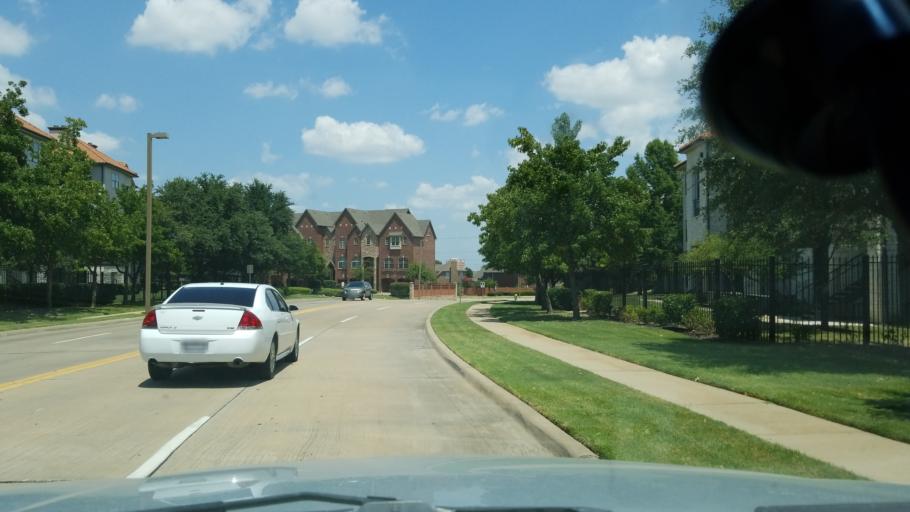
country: US
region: Texas
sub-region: Dallas County
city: Farmers Branch
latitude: 32.9166
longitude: -96.9520
